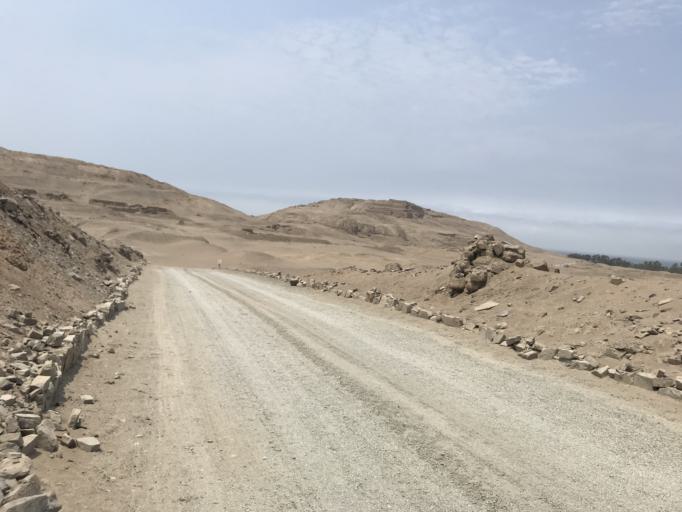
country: PE
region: Lima
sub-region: Lima
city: Punta Hermosa
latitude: -12.2569
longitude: -76.8971
